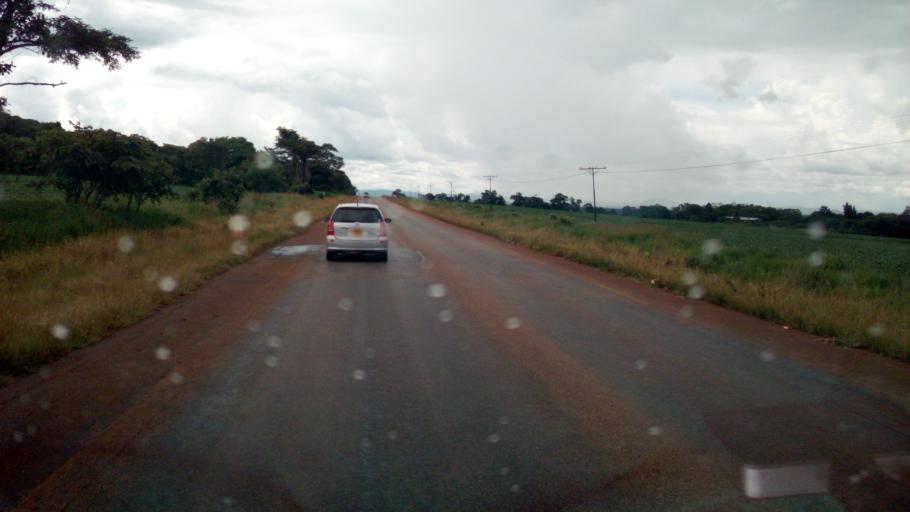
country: ZW
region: Mashonaland Central
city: Glendale
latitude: -17.3307
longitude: 31.1565
